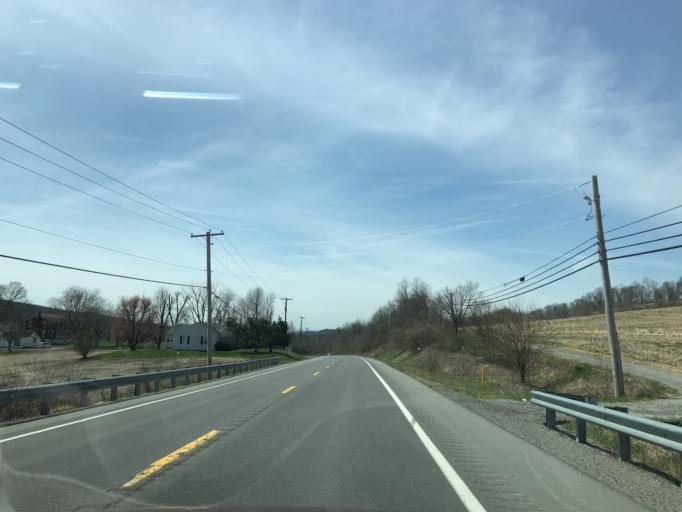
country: US
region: Pennsylvania
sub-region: Snyder County
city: Selinsgrove
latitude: 40.8069
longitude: -76.9505
